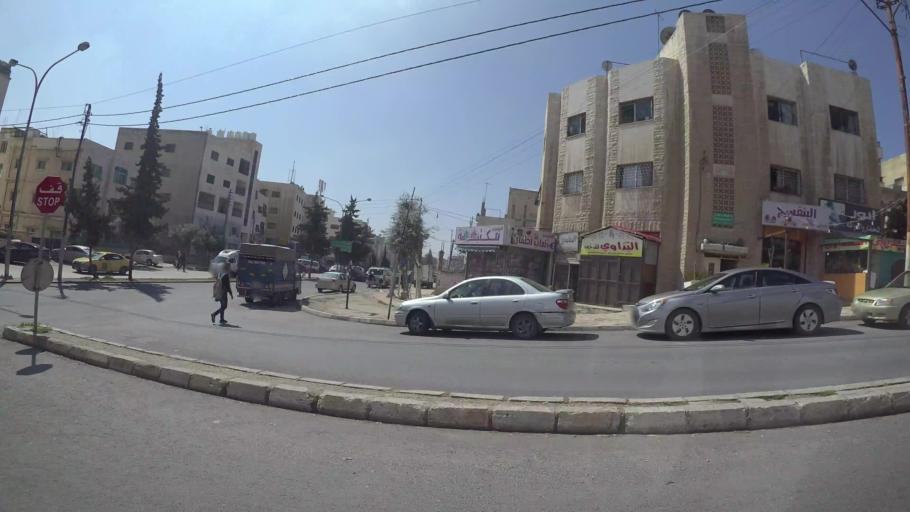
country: JO
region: Amman
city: Al Bunayyat ash Shamaliyah
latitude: 31.9273
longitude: 35.9059
